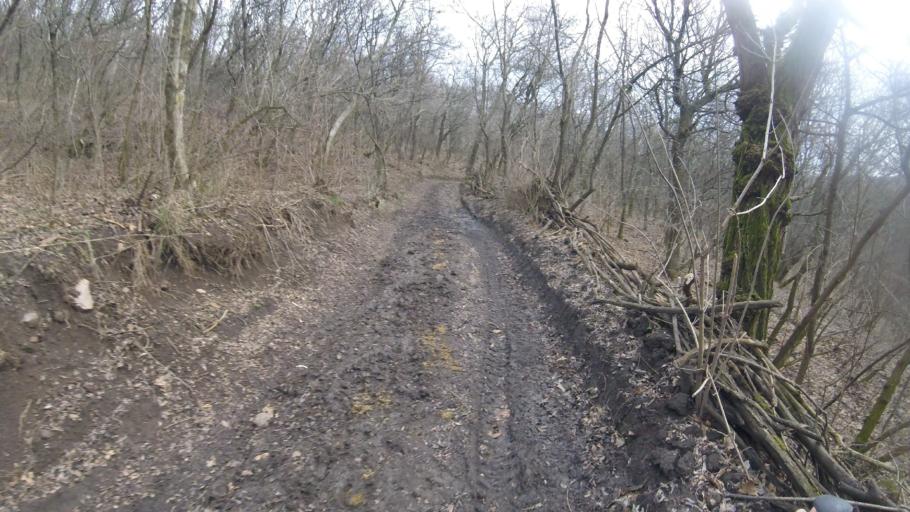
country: HU
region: Pest
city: Nagykovacsi
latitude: 47.6723
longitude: 19.0118
